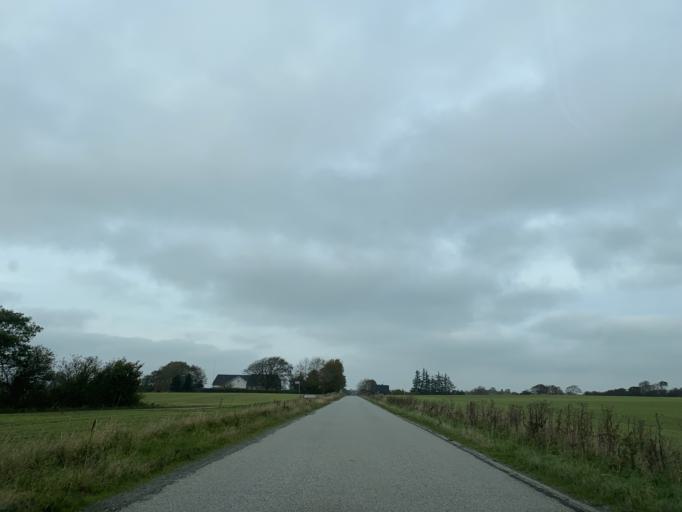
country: DK
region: South Denmark
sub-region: Haderslev Kommune
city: Starup
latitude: 55.1727
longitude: 9.5180
